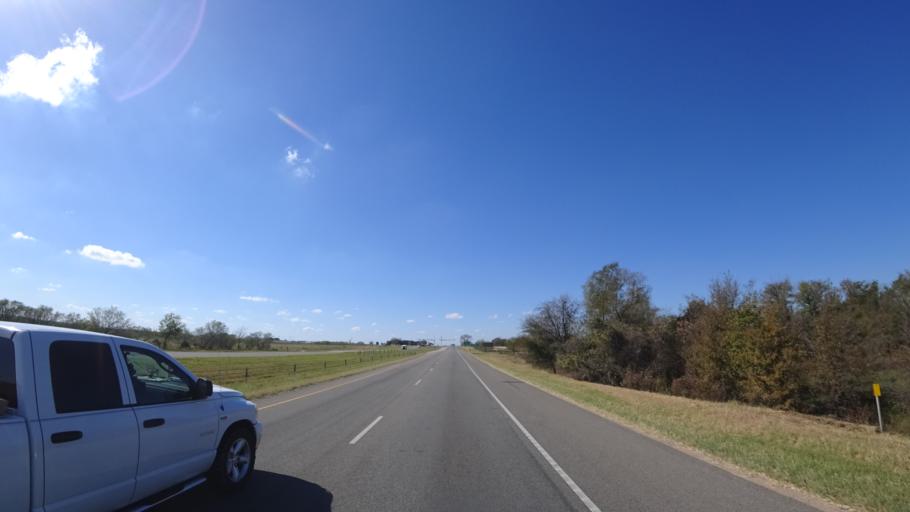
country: US
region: Texas
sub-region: Travis County
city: Garfield
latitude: 30.1883
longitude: -97.5942
